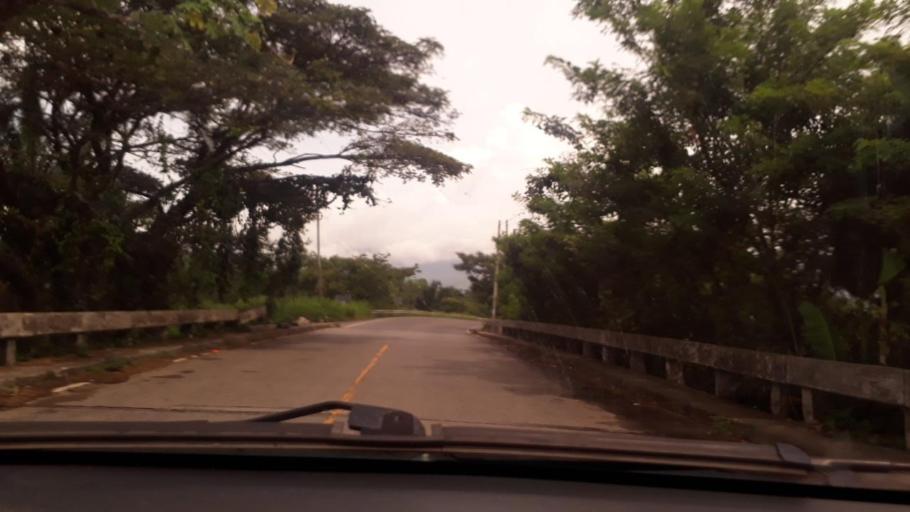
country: HN
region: Cortes
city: Potrerillos
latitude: 15.6340
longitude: -88.4060
